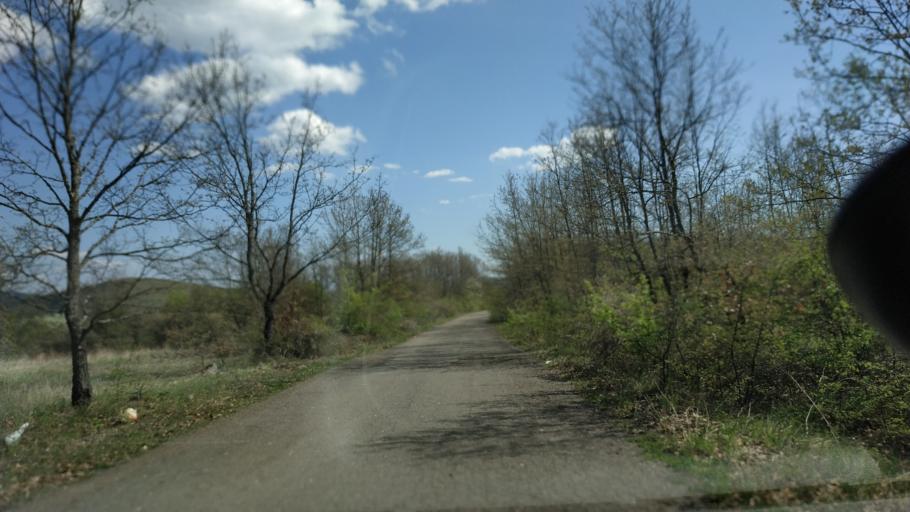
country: RS
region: Central Serbia
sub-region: Zajecarski Okrug
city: Soko Banja
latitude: 43.5423
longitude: 21.9029
